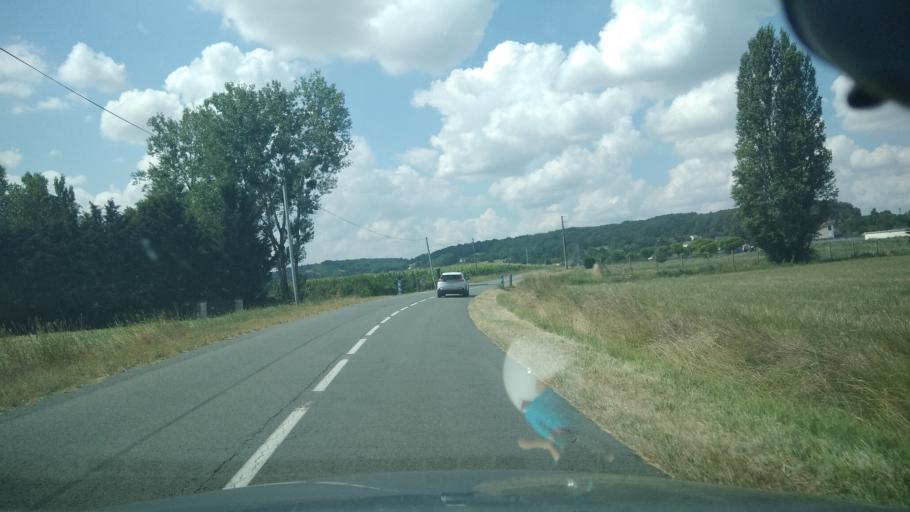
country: FR
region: Poitou-Charentes
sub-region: Departement de la Vienne
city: Dange-Saint-Romain
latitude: 46.9142
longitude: 0.5766
